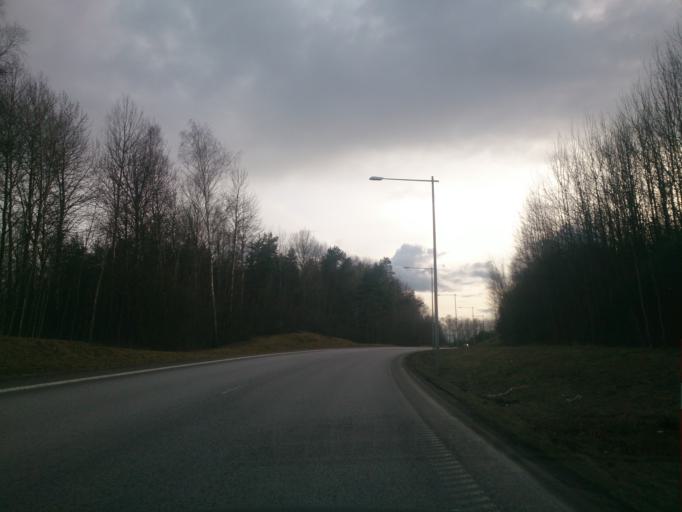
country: SE
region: OEstergoetland
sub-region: Norrkopings Kommun
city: Jursla
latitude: 58.6365
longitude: 16.1607
